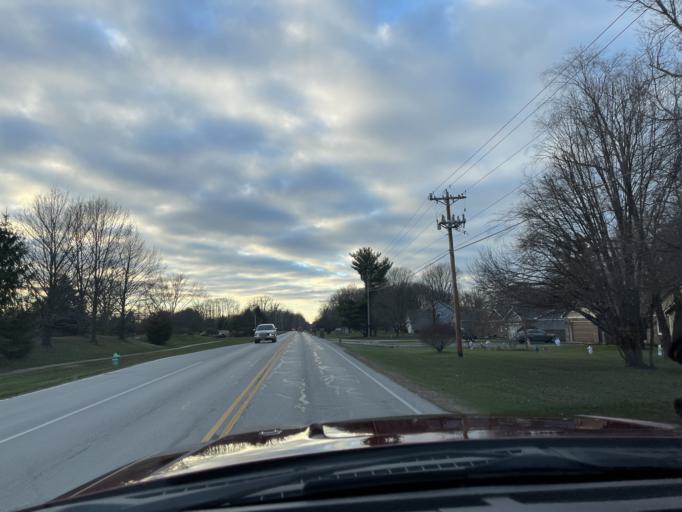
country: US
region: Indiana
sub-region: Hendricks County
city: Avon
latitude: 39.7772
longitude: -86.4073
